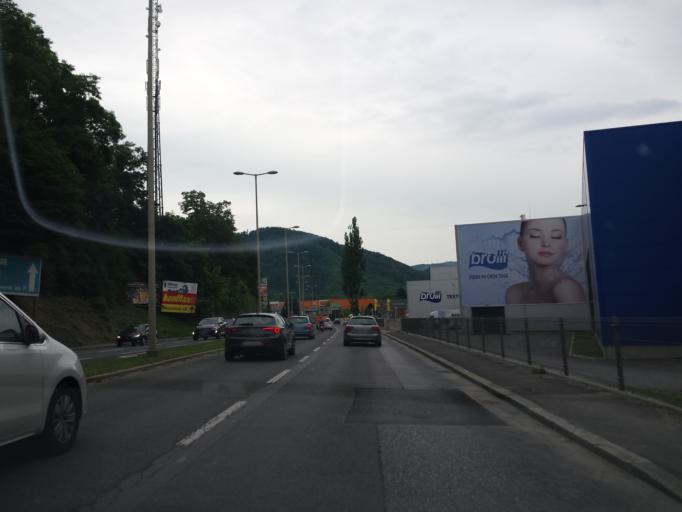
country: AT
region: Styria
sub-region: Graz Stadt
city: Goesting
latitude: 47.1011
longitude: 15.4033
